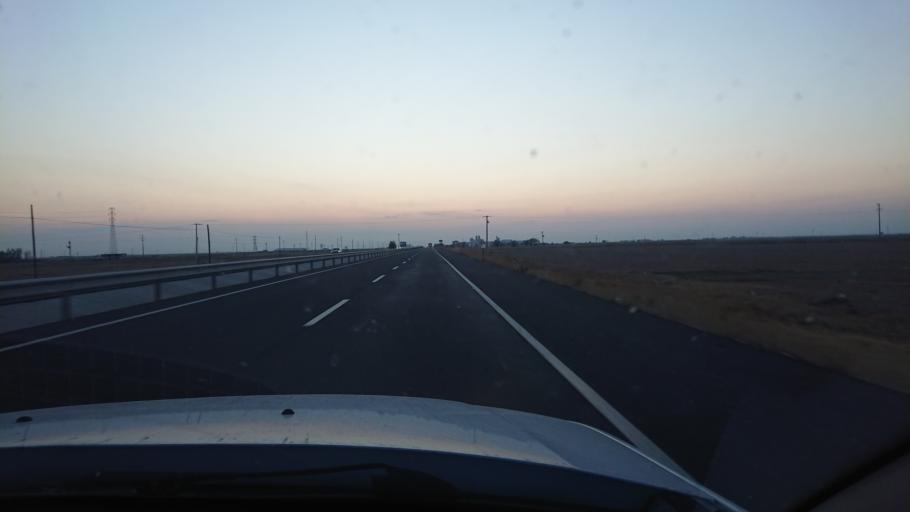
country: TR
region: Aksaray
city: Yesilova
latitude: 38.3179
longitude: 33.8567
